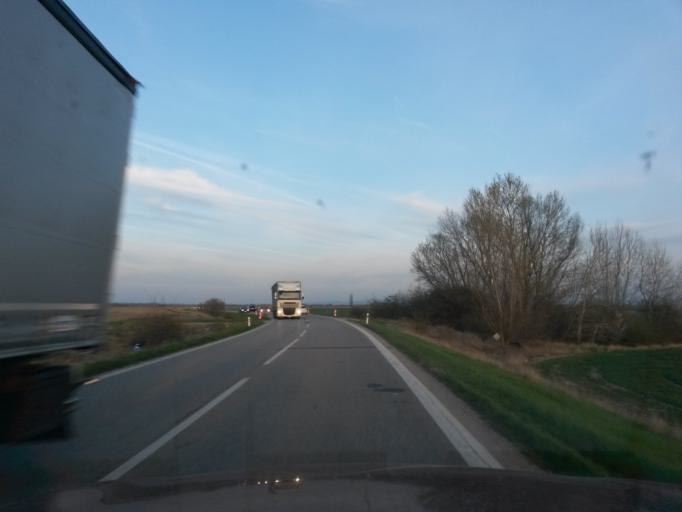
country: SK
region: Nitriansky
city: Komarno
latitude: 47.7652
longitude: 18.1668
